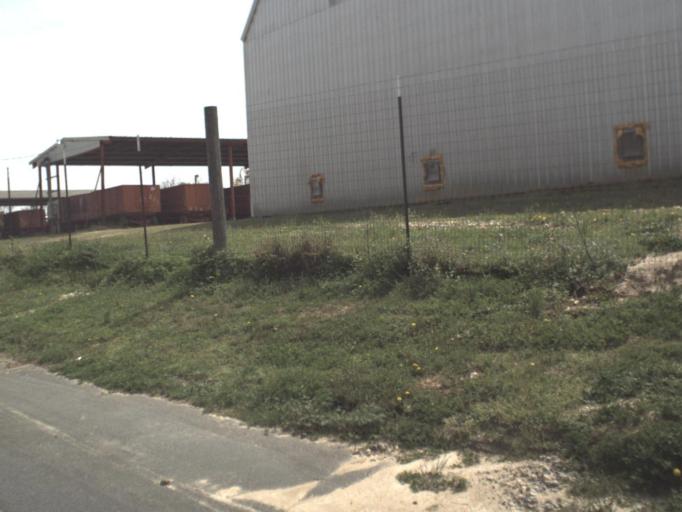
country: US
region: Florida
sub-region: Jackson County
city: Graceville
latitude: 30.9512
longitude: -85.4059
